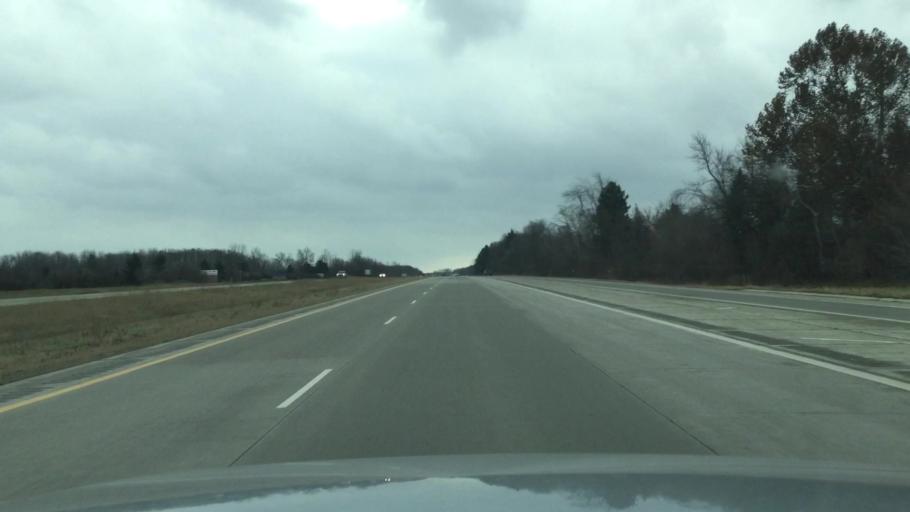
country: US
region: Michigan
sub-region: Genesee County
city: Grand Blanc
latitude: 42.9420
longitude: -83.6817
